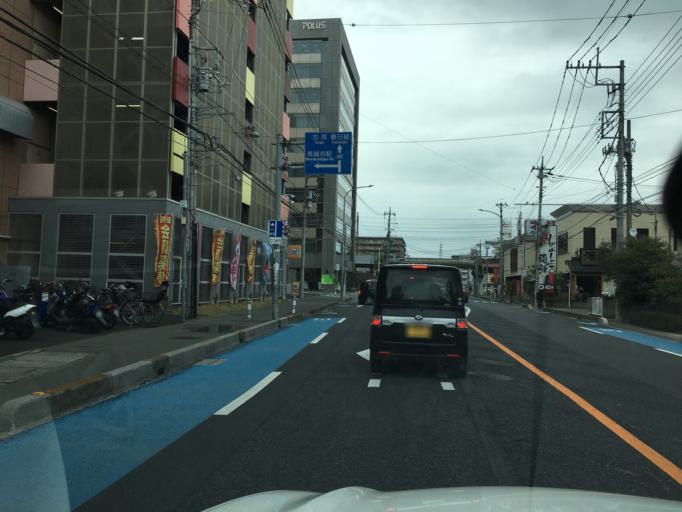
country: JP
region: Saitama
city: Koshigaya
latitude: 35.8748
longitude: 139.7936
